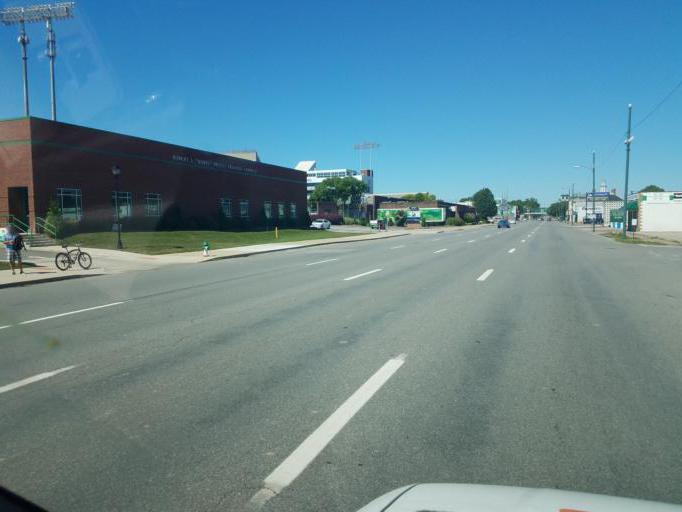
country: US
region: West Virginia
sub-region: Cabell County
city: Huntington
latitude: 38.4263
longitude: -82.4195
